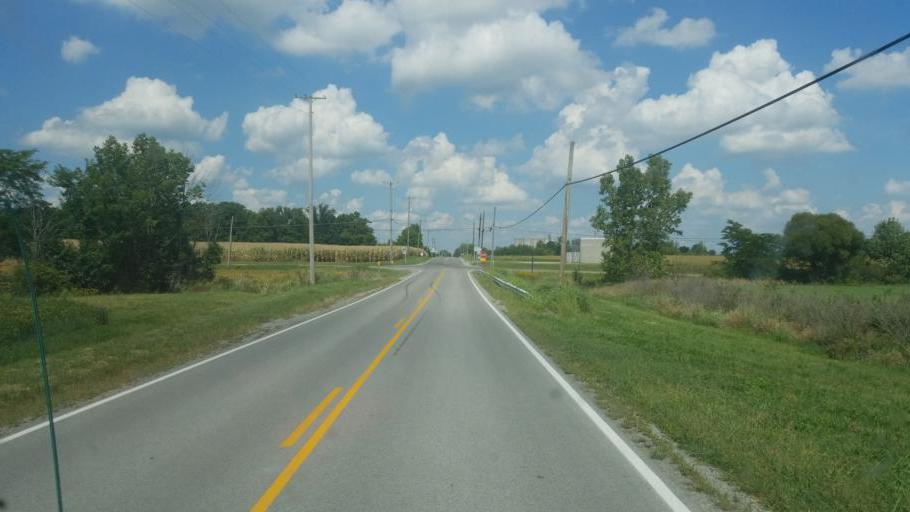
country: US
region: Ohio
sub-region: Hancock County
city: Arlington
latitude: 40.8912
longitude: -83.7271
